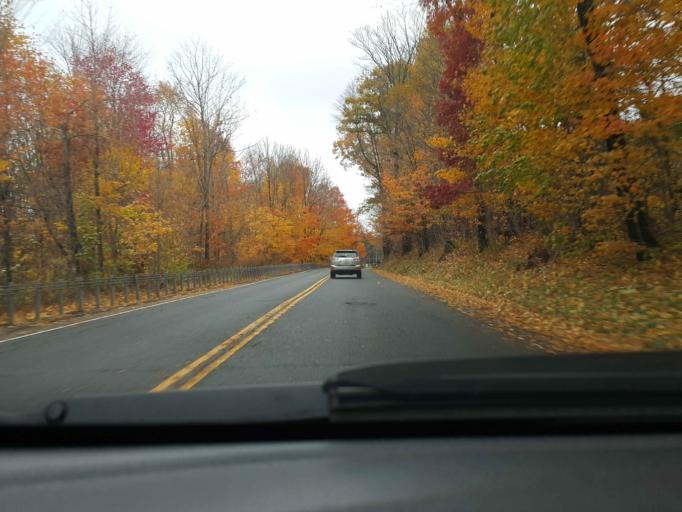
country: US
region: Connecticut
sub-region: Middlesex County
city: Durham
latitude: 41.5217
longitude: -72.6672
